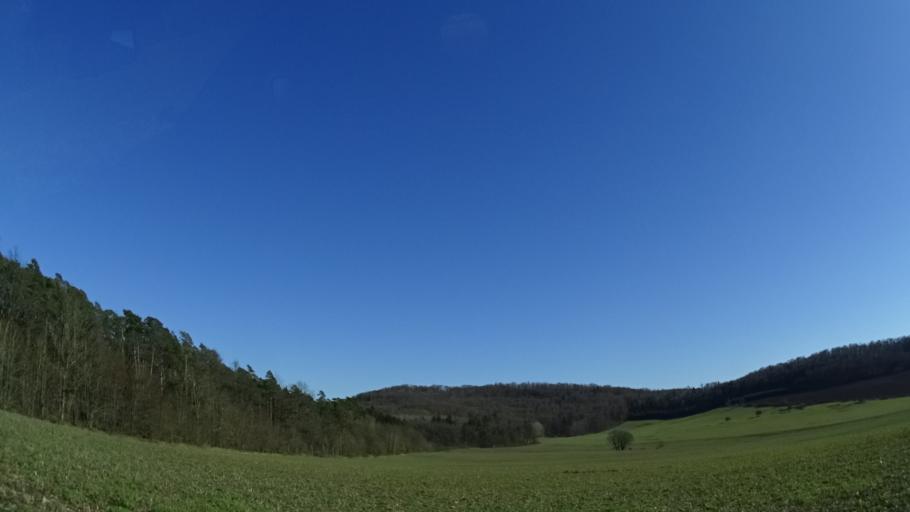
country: DE
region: Bavaria
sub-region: Regierungsbezirk Unterfranken
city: Willmars
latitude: 50.4938
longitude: 10.2898
